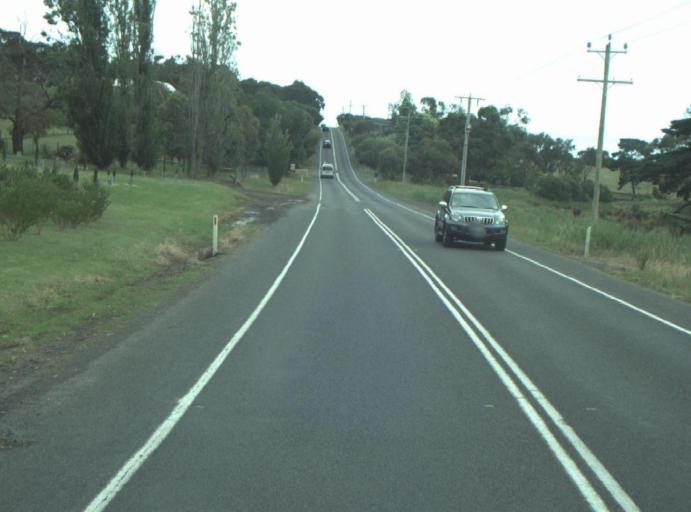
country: AU
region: Victoria
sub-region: Greater Geelong
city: Leopold
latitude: -38.2133
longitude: 144.5069
